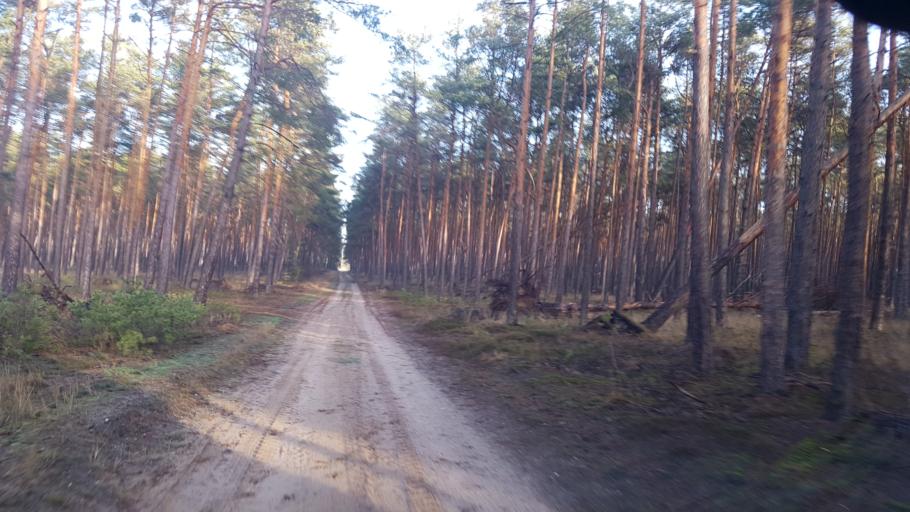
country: DE
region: Brandenburg
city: Schilda
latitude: 51.6341
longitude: 13.3963
